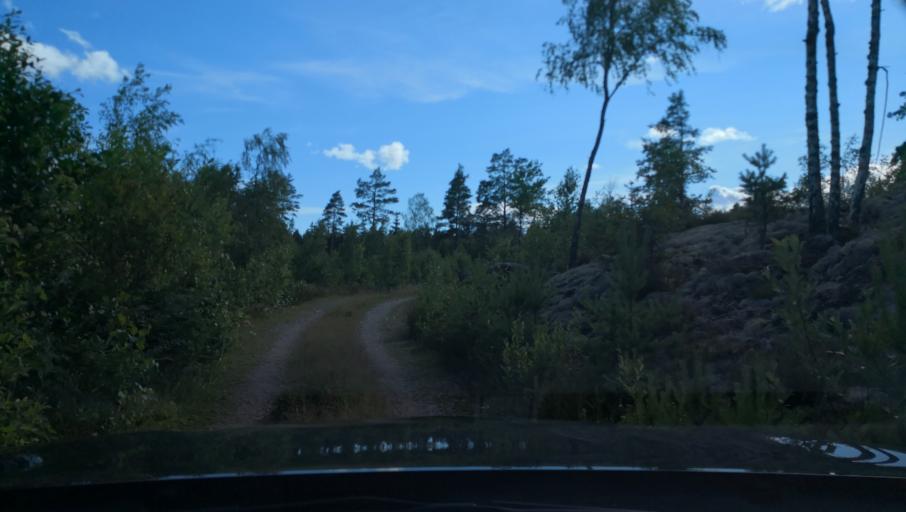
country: SE
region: Vaestmanland
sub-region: Surahammars Kommun
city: Surahammar
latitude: 59.6809
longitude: 16.2651
